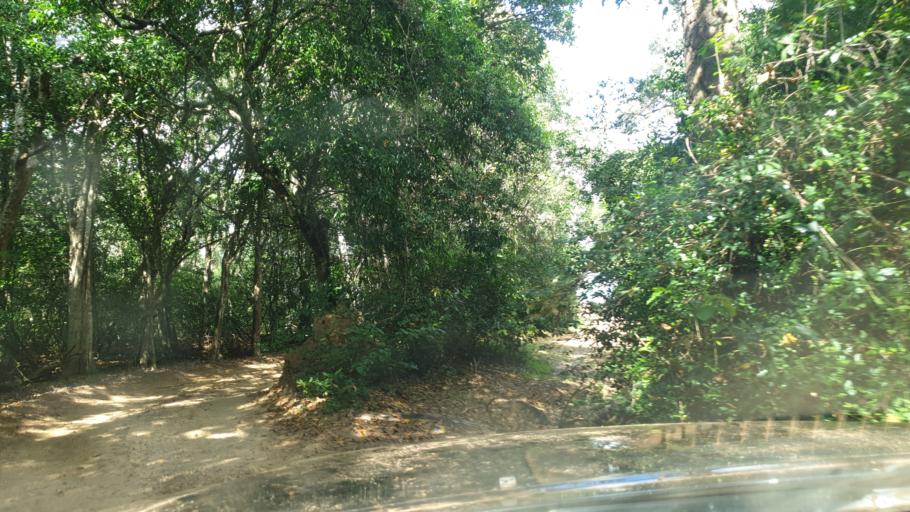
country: LK
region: North Central
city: Anuradhapura
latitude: 8.4232
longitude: 80.0112
